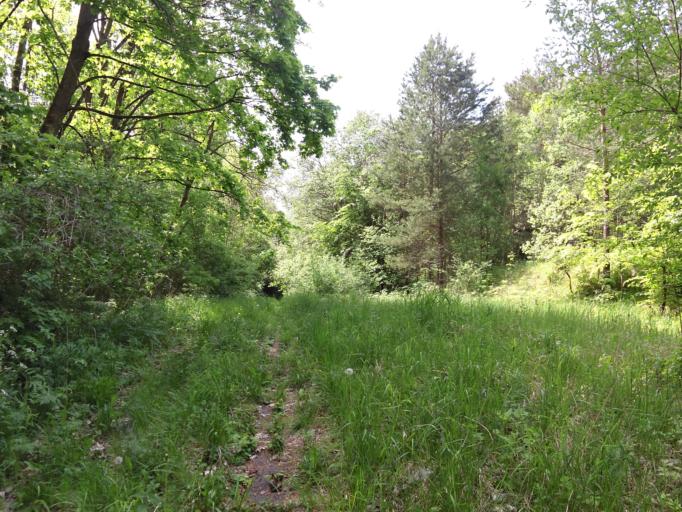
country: DE
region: Thuringia
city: Ifta
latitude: 51.0606
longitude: 10.1467
